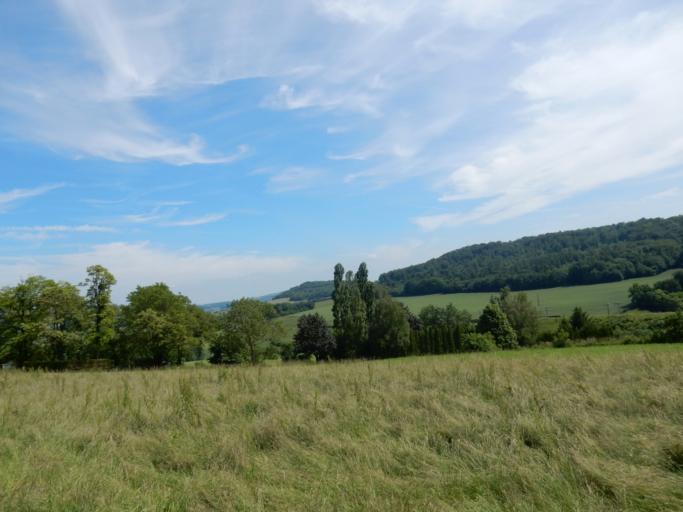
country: FR
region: Lorraine
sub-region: Departement de Meurthe-et-Moselle
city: Pagny-sur-Moselle
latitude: 48.9748
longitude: 5.9900
